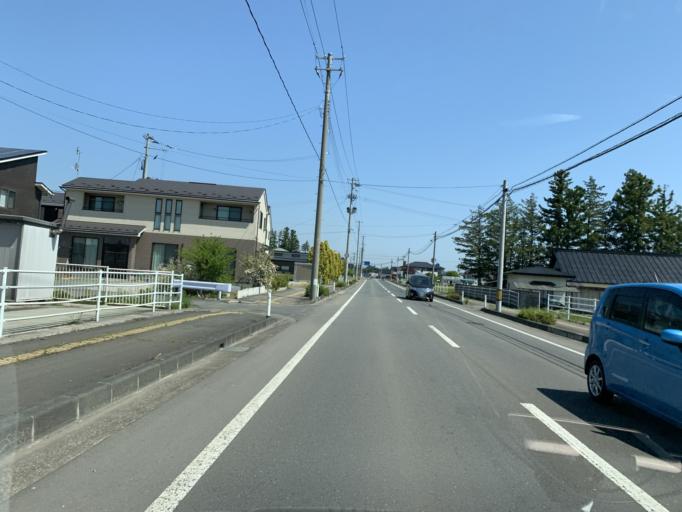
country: JP
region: Iwate
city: Mizusawa
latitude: 39.1937
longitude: 141.0949
